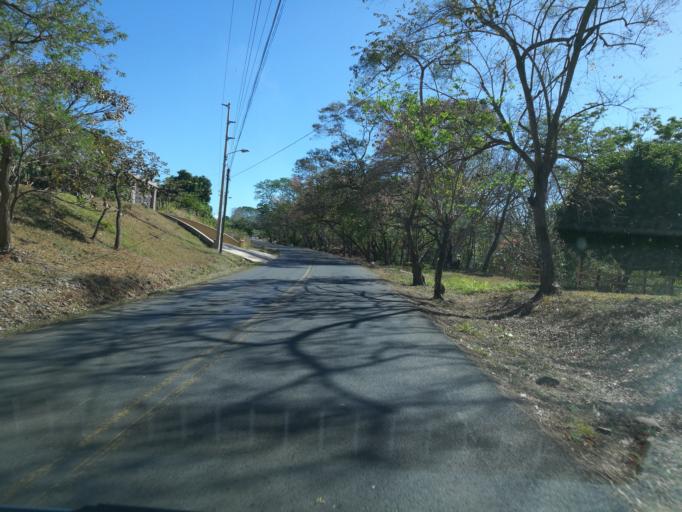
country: CR
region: Puntarenas
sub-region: Canton Central de Puntarenas
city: Puntarenas
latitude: 10.1083
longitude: -84.9058
